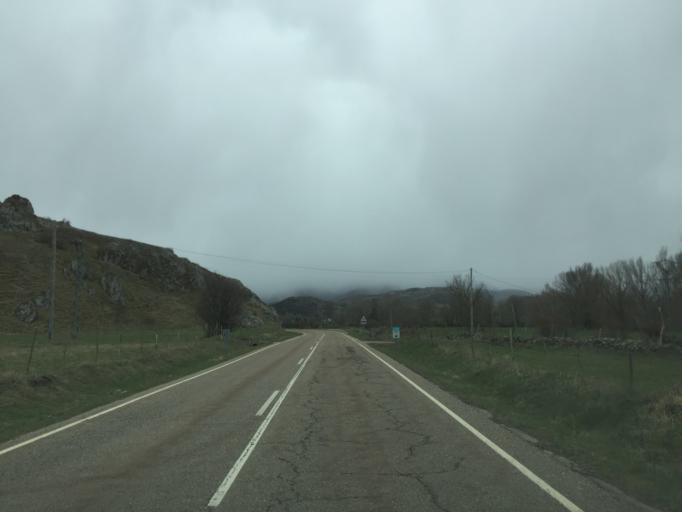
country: ES
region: Castille and Leon
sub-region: Provincia de Leon
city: San Emiliano
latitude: 42.9828
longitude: -6.0012
